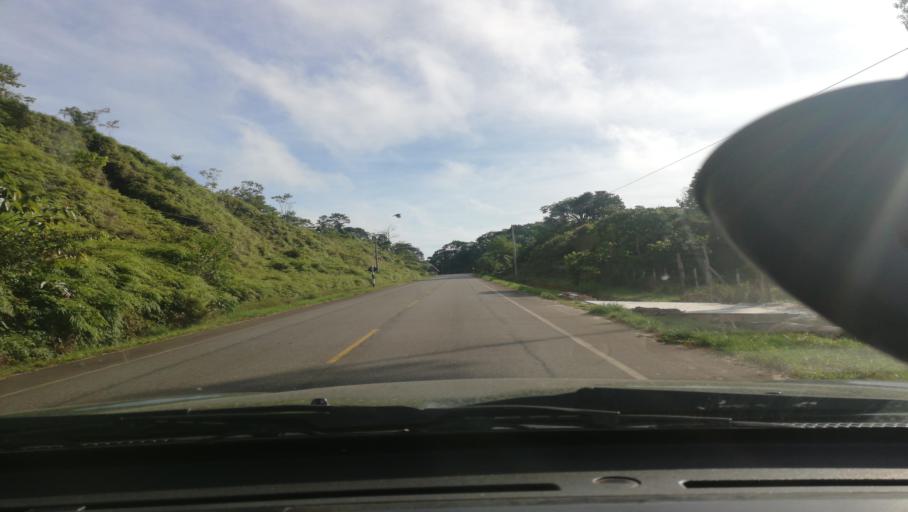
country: PE
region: Loreto
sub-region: Provincia de Loreto
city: Nauta
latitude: -4.4194
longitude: -73.5849
